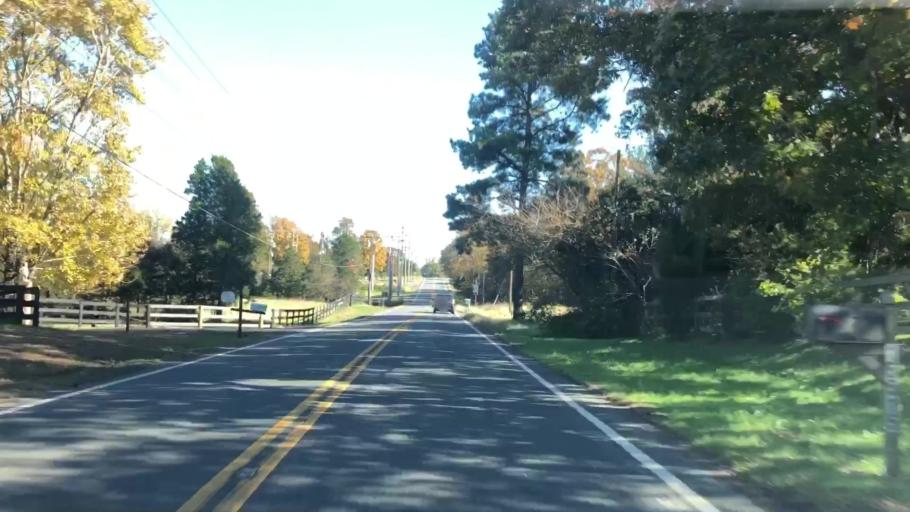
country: US
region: Virginia
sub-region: Prince William County
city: Gainesville
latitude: 38.7514
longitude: -77.6564
